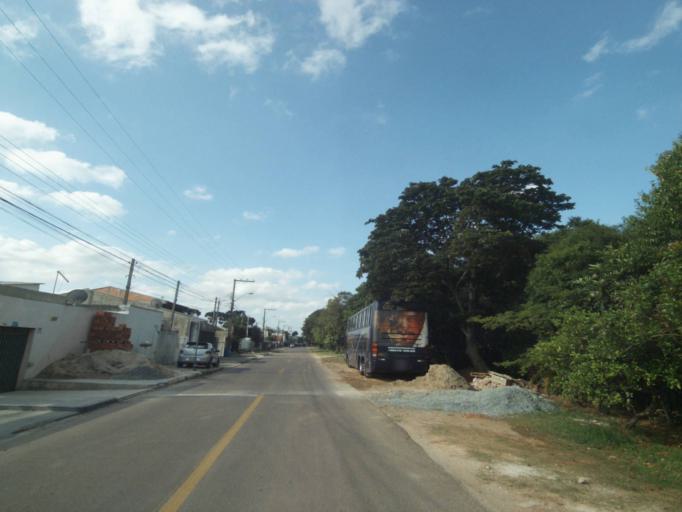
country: BR
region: Parana
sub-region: Curitiba
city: Curitiba
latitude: -25.5039
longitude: -49.3263
